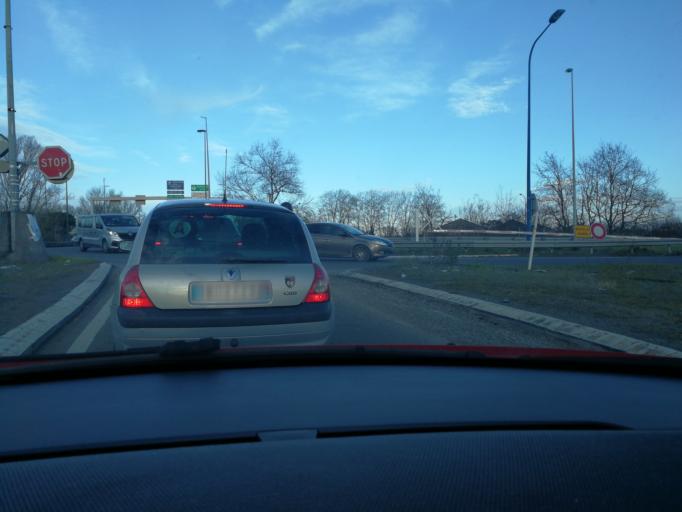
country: FR
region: Midi-Pyrenees
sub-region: Departement de la Haute-Garonne
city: Aucamville
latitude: 43.6473
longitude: 1.4199
